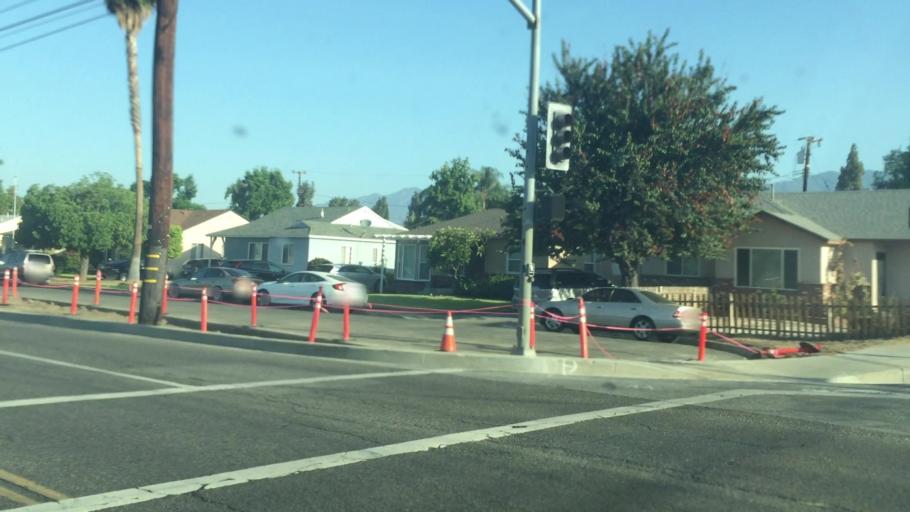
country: US
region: California
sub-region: Los Angeles County
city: Irwindale
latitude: 34.0960
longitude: -117.9256
